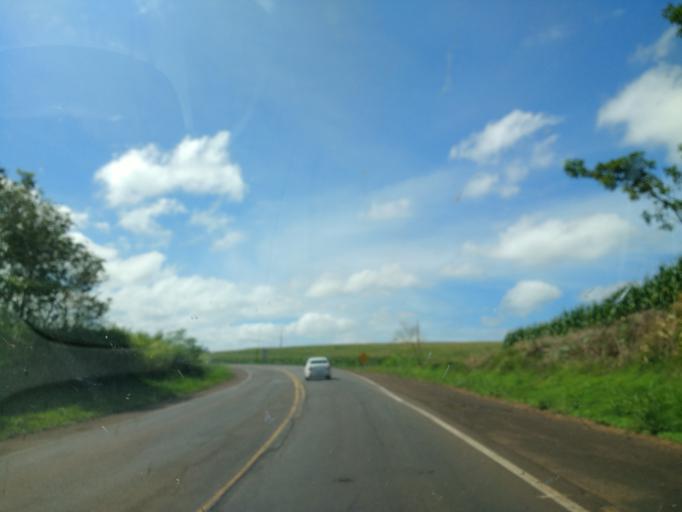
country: BR
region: Parana
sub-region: Cianorte
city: Cianorte
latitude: -23.6563
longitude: -52.5046
